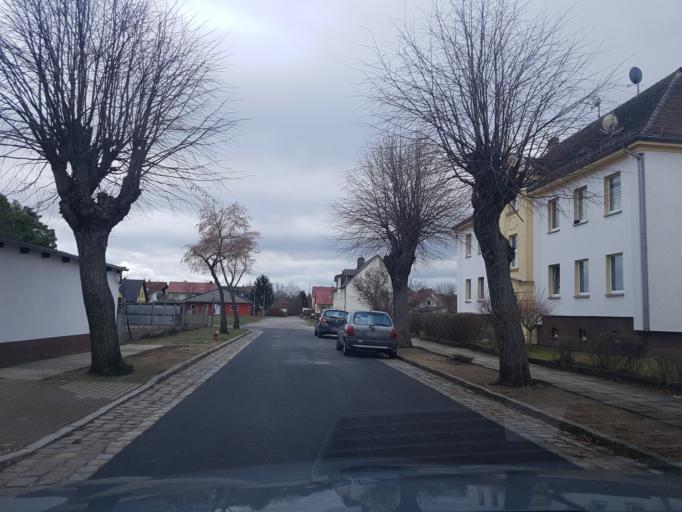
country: DE
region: Brandenburg
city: Falkenberg
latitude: 51.5866
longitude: 13.2549
